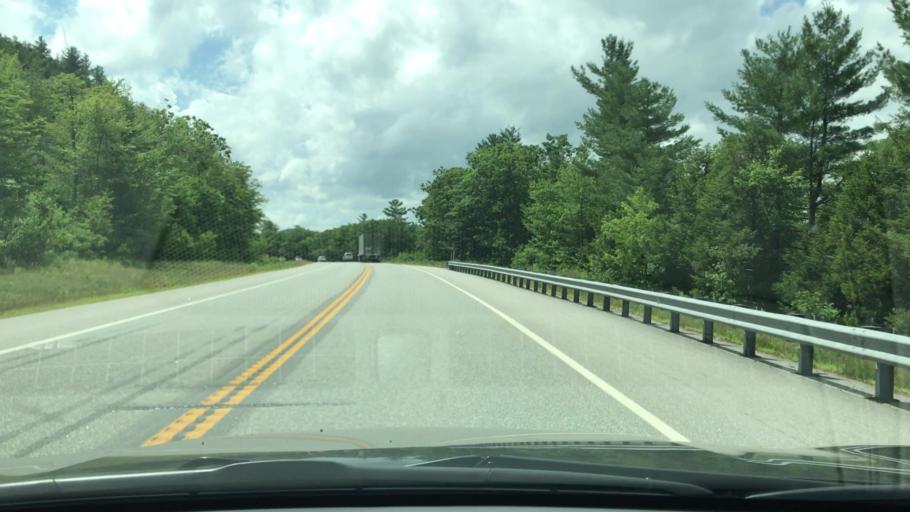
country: US
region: Maine
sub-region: Oxford County
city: Bethel
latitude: 44.3979
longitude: -70.9467
